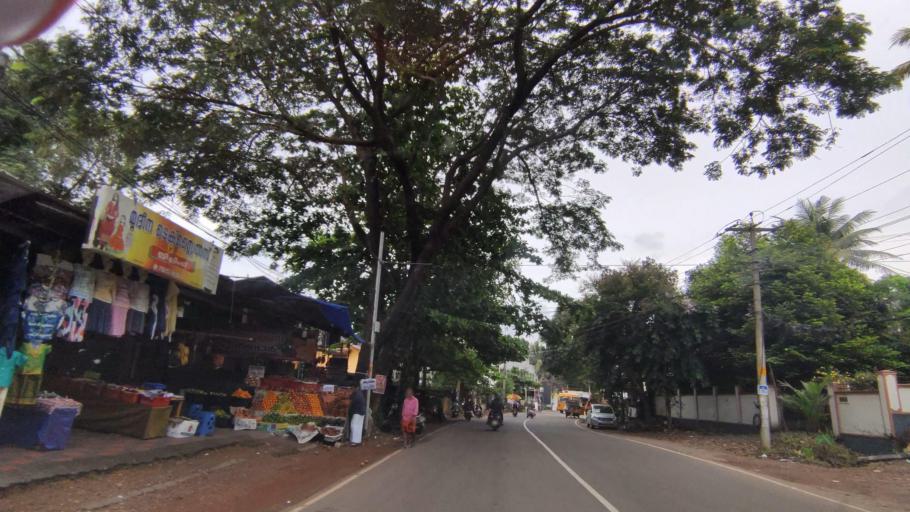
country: IN
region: Kerala
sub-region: Kottayam
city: Kottayam
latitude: 9.6148
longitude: 76.5077
